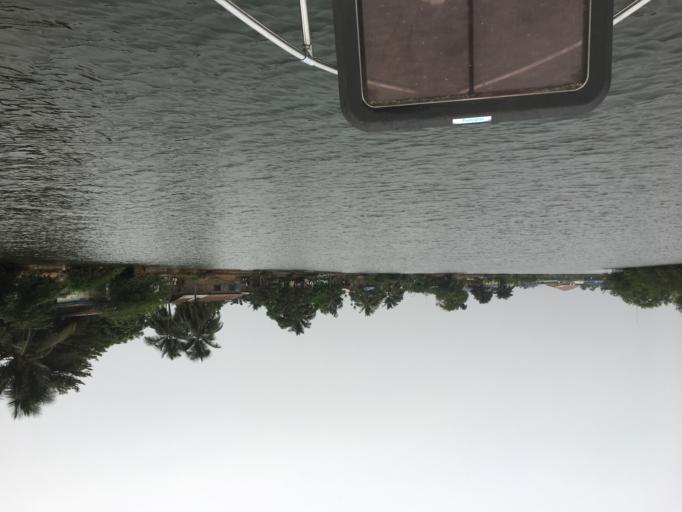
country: LR
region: Montserrado
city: Monrovia
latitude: 6.3867
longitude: -10.7792
